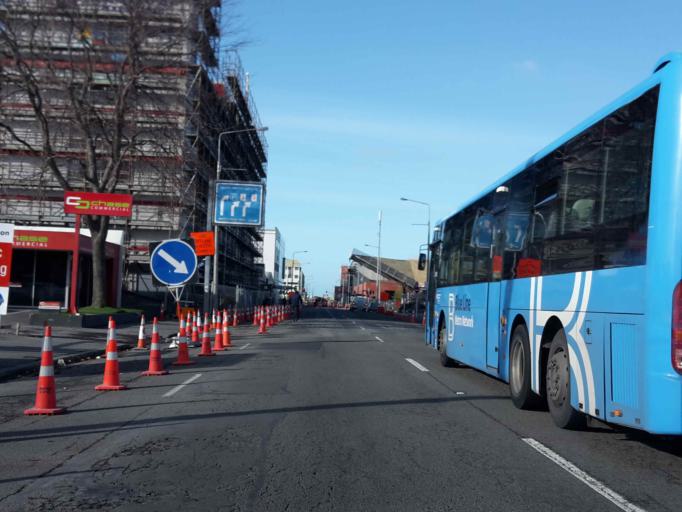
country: NZ
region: Canterbury
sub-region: Christchurch City
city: Christchurch
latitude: -43.5342
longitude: 172.6342
